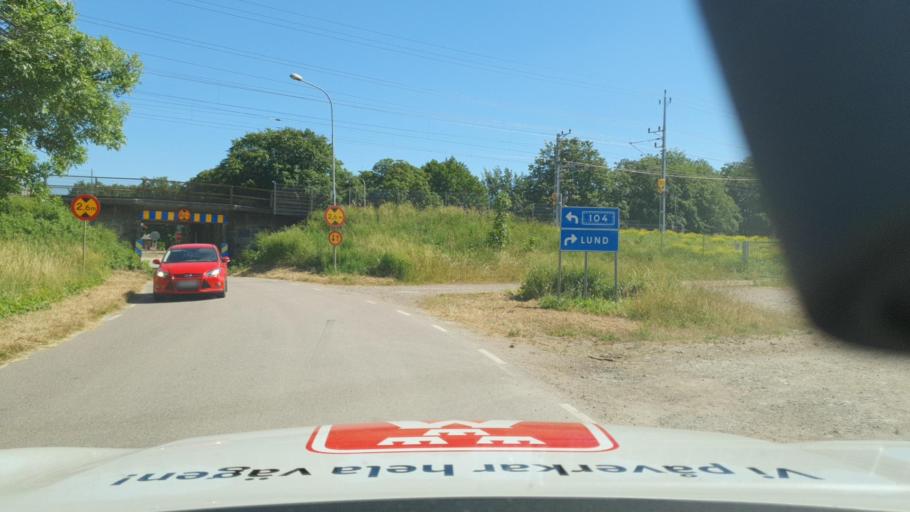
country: SE
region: Skane
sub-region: Eslovs Kommun
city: Eslov
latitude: 55.7826
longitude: 13.2511
